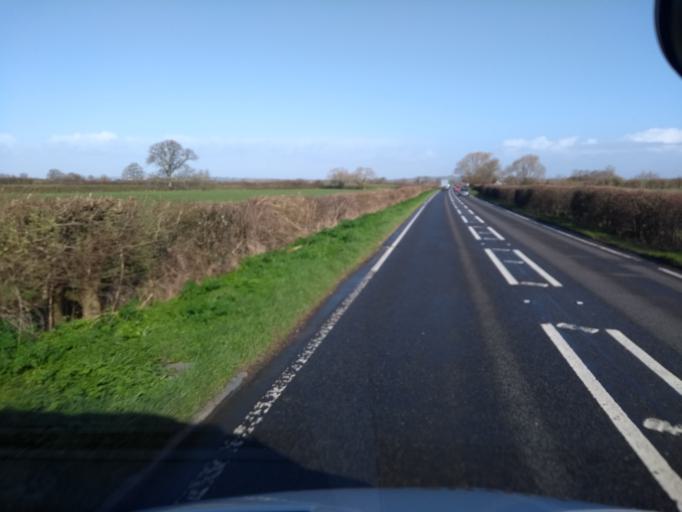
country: GB
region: England
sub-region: Somerset
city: Ilchester
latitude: 50.9801
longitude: -2.6743
